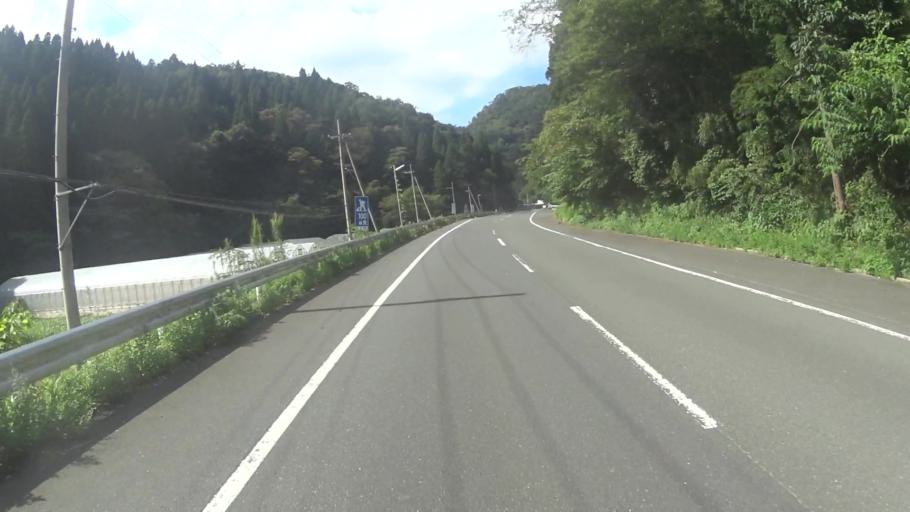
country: JP
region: Kyoto
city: Miyazu
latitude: 35.7341
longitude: 135.2563
